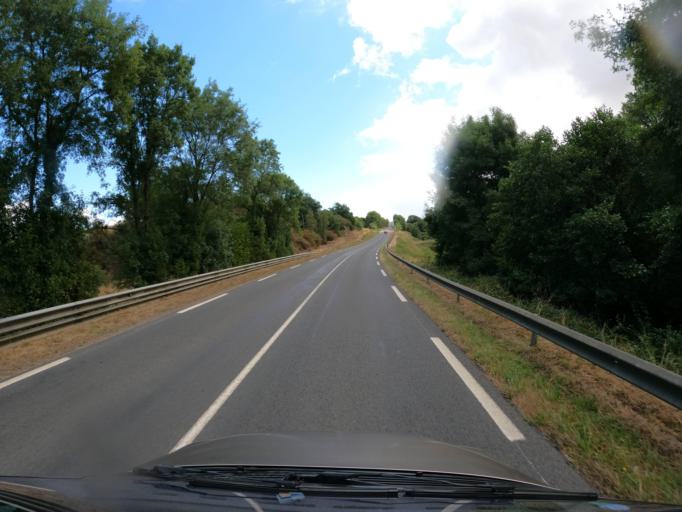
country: FR
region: Pays de la Loire
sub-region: Departement de la Loire-Atlantique
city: La Remaudiere
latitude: 47.2294
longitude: -1.2246
